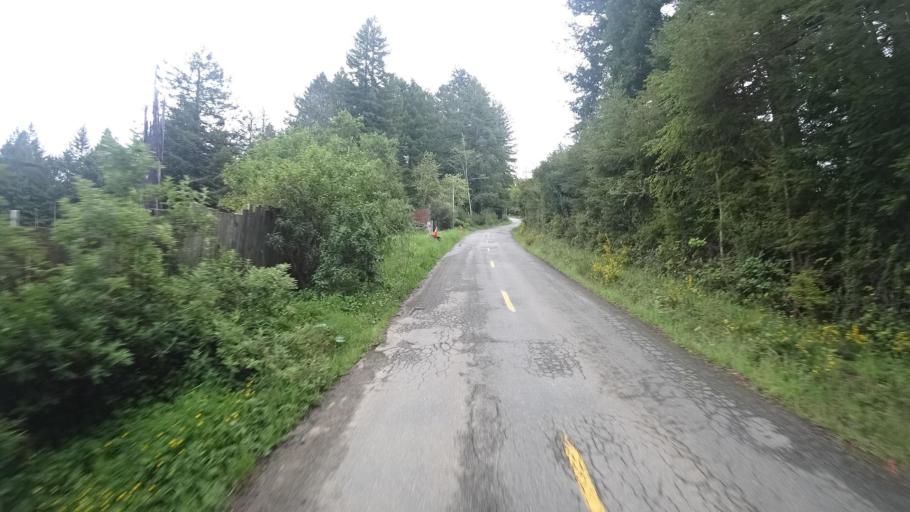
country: US
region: California
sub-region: Humboldt County
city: Bayside
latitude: 40.7885
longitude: -124.0166
